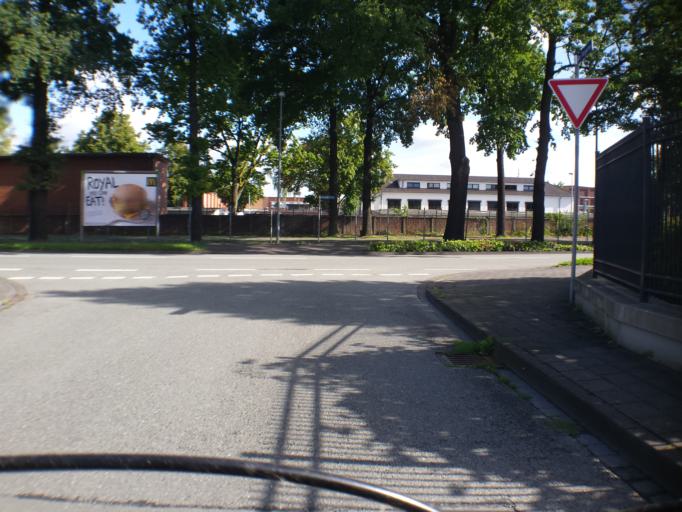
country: DE
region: North Rhine-Westphalia
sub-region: Regierungsbezirk Arnsberg
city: Lippstadt
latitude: 51.6800
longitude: 8.3153
